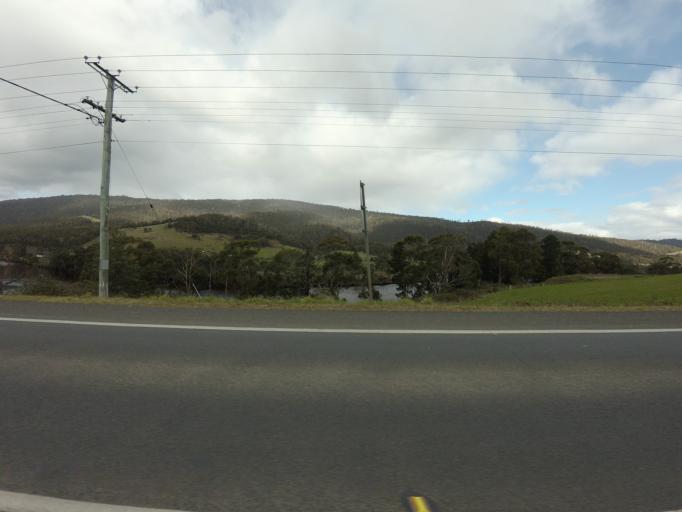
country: AU
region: Tasmania
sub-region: Huon Valley
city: Huonville
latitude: -43.0449
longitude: 147.0428
